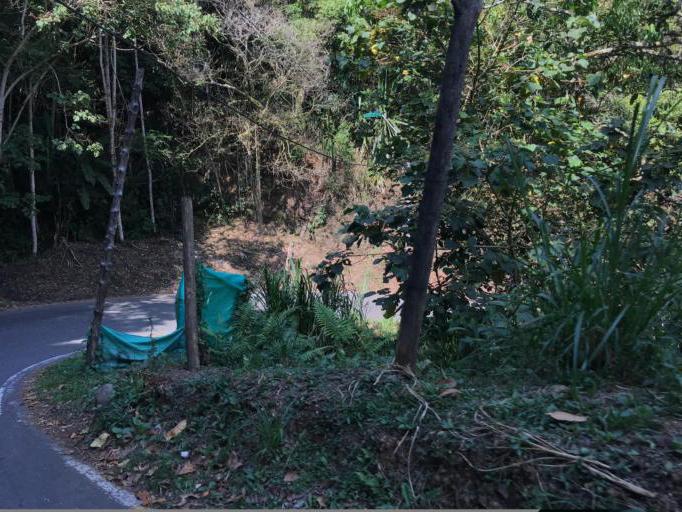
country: CO
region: Valle del Cauca
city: Cali
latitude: 3.4793
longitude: -76.6134
